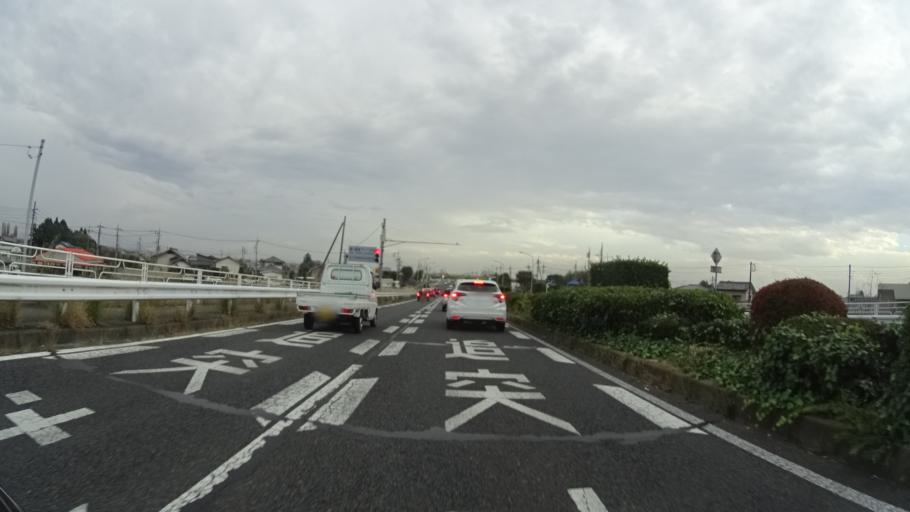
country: JP
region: Gunma
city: Maebashi-shi
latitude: 36.3735
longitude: 139.1274
